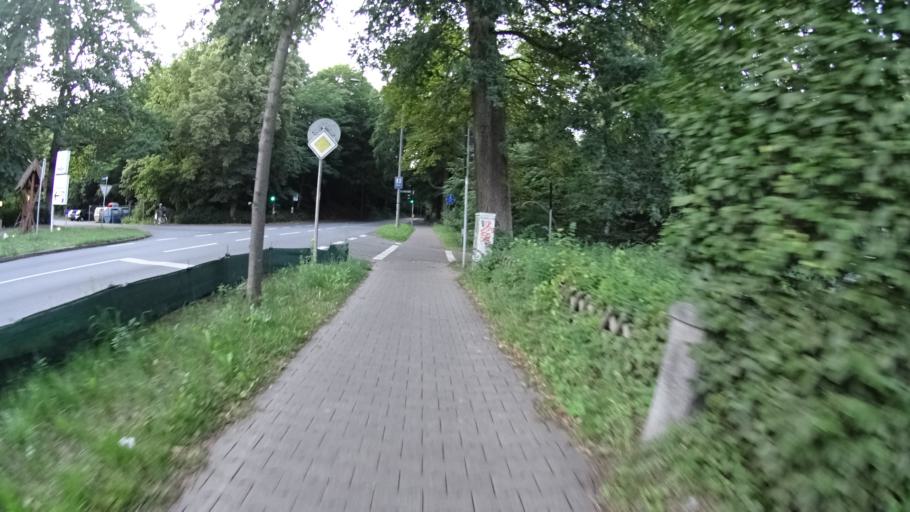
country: DE
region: Lower Saxony
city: Lueneburg
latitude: 53.2252
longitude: 10.3941
